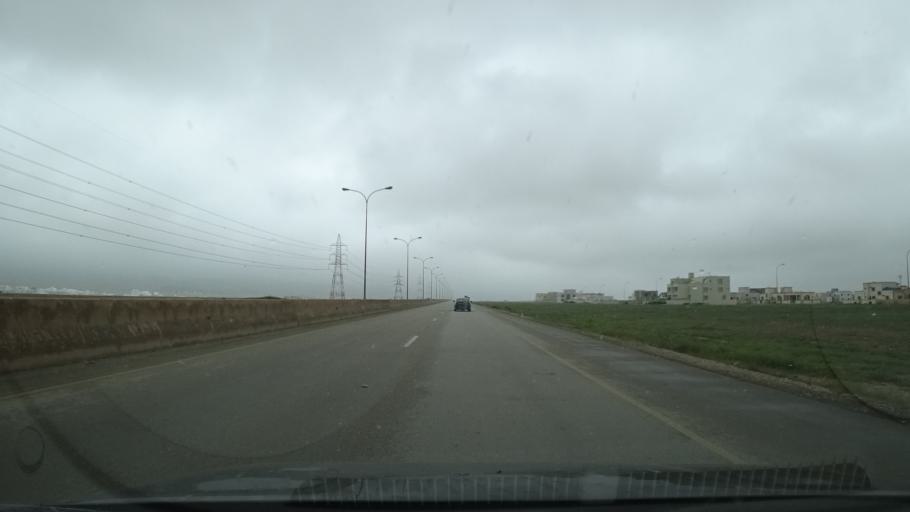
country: OM
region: Zufar
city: Salalah
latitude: 17.1039
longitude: 54.2056
